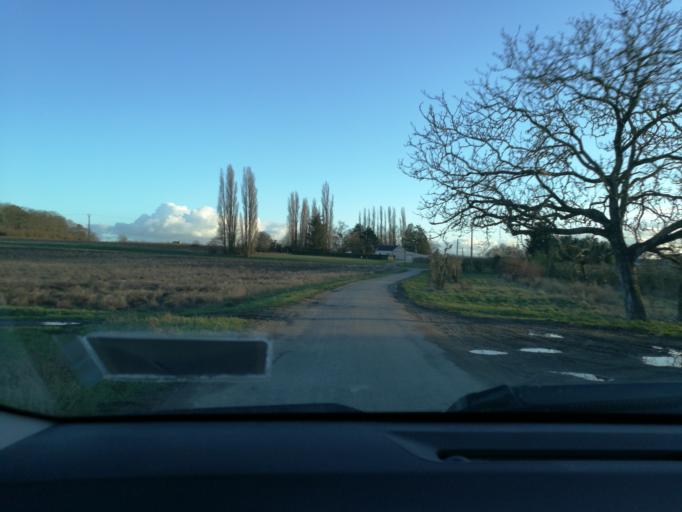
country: FR
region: Centre
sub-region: Departement du Loiret
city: Semoy
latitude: 47.9337
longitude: 1.9704
